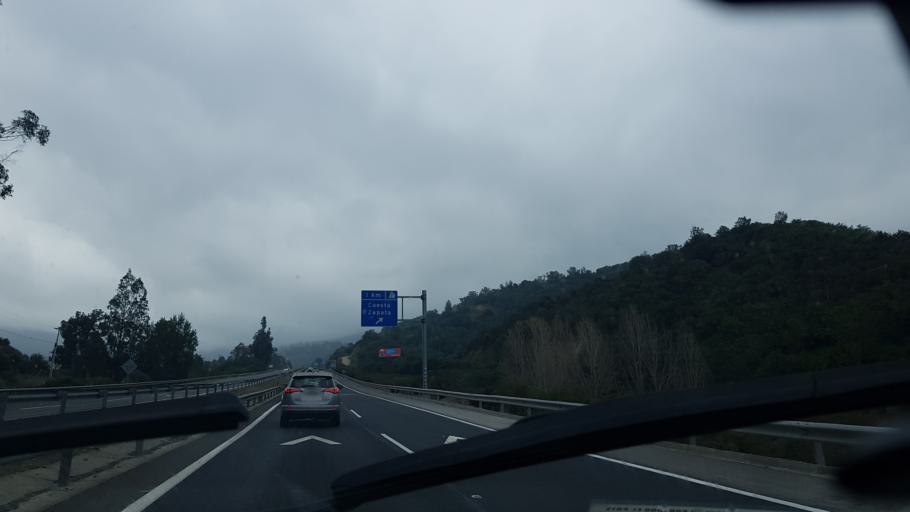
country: CL
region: Santiago Metropolitan
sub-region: Provincia de Melipilla
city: Melipilla
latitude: -33.4016
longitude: -71.2205
